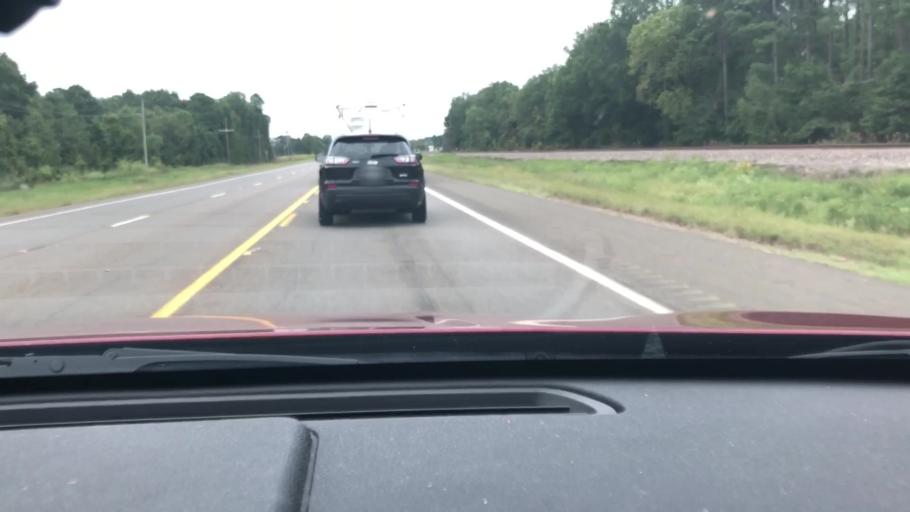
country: US
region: Arkansas
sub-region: Lafayette County
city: Lewisville
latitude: 33.3570
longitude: -93.5952
